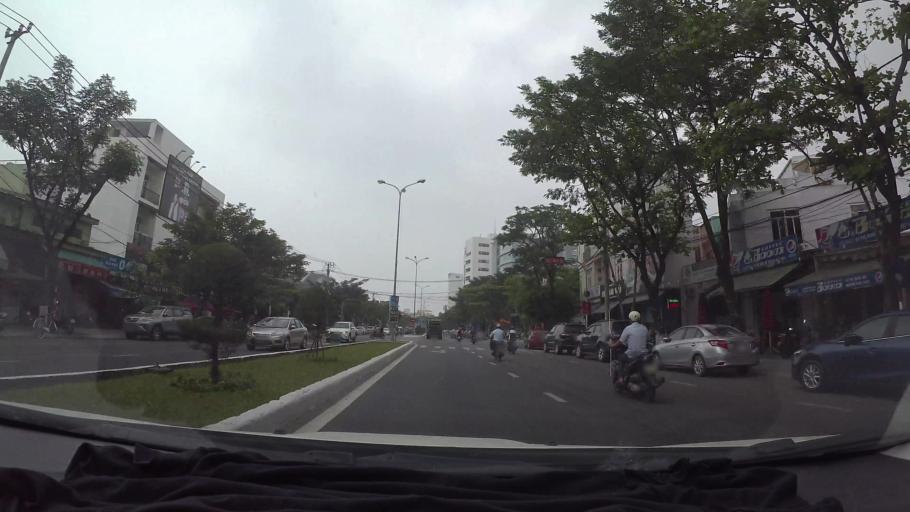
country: VN
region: Da Nang
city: Da Nang
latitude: 16.0523
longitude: 108.2090
